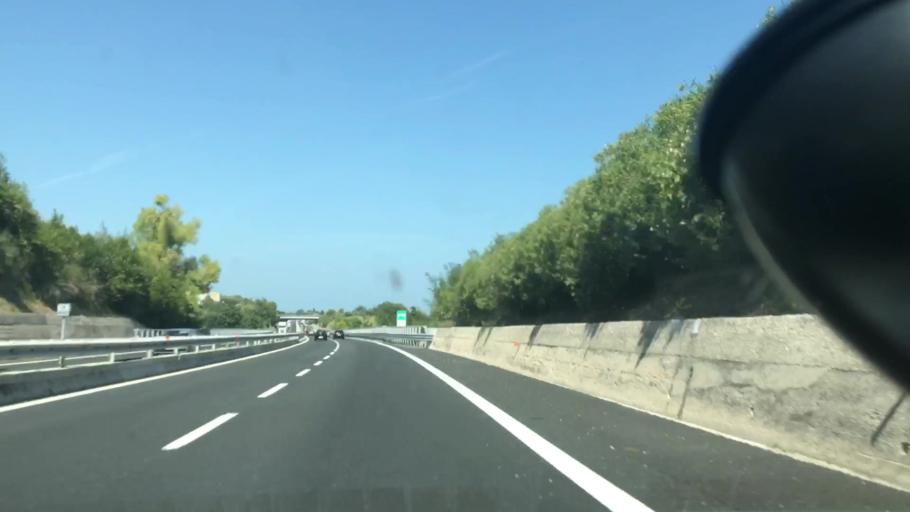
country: IT
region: Abruzzo
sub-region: Provincia di Chieti
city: Ortona
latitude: 42.3460
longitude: 14.3568
